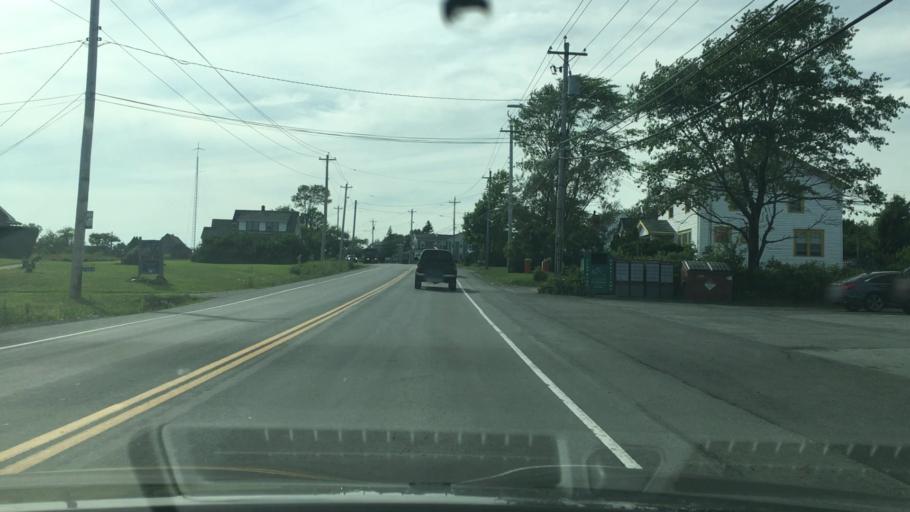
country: CA
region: Nova Scotia
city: Dartmouth
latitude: 44.7330
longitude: -63.7617
